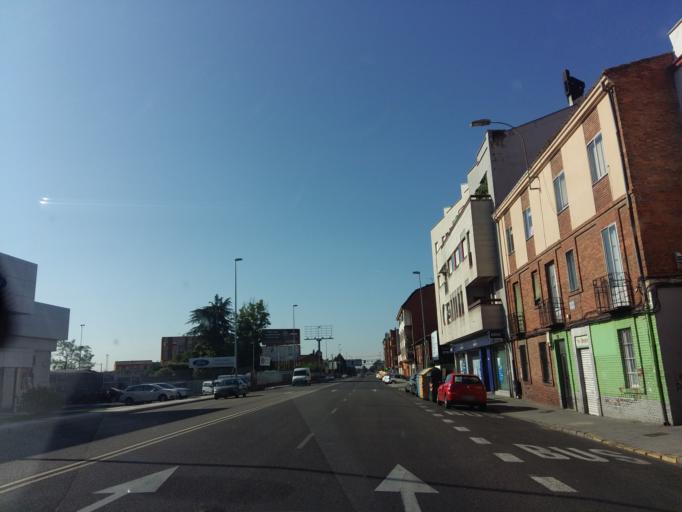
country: ES
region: Castille and Leon
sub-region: Provincia de Leon
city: Leon
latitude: 42.5846
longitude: -5.5843
